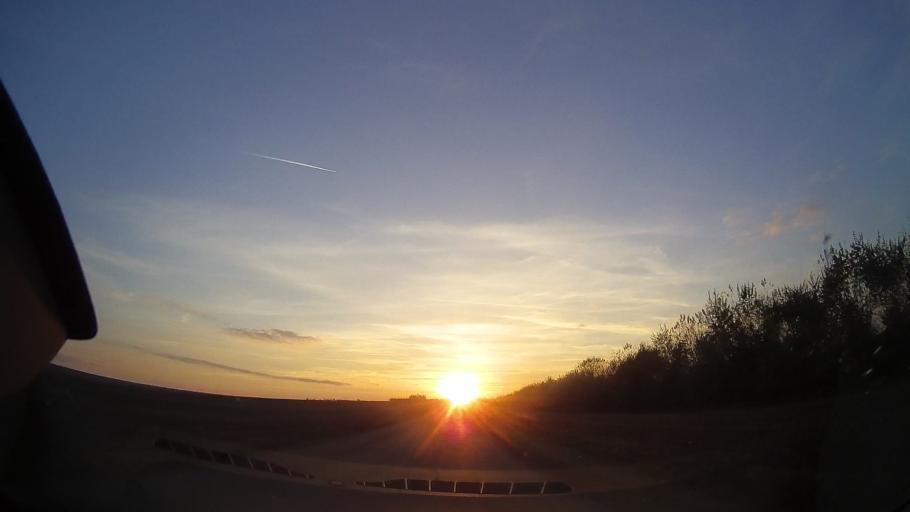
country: RO
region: Constanta
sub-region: Comuna Mereni
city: Mereni
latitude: 44.0262
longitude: 28.3658
